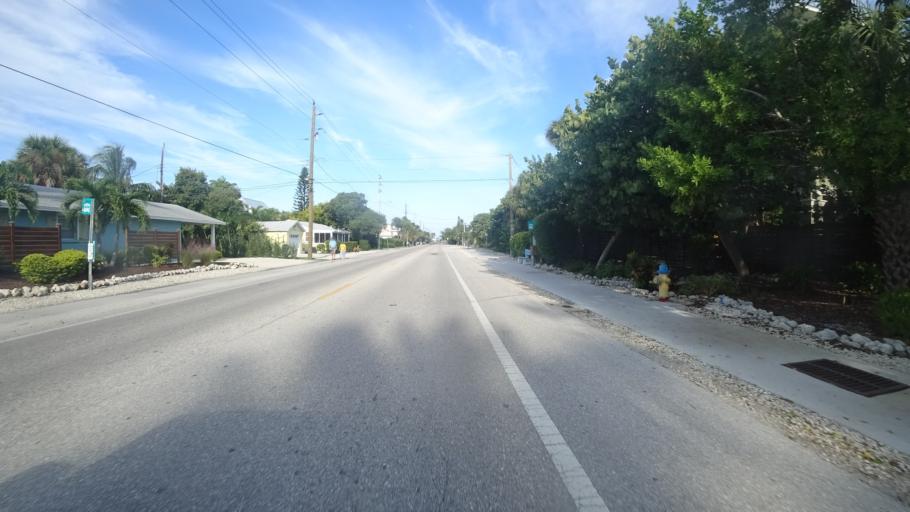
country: US
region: Florida
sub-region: Manatee County
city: Anna Maria
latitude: 27.5231
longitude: -82.7310
